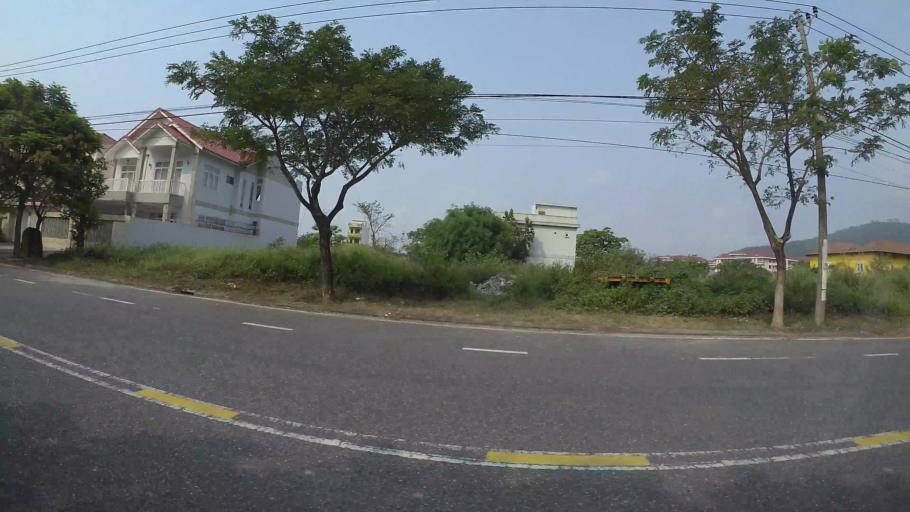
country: VN
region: Da Nang
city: Son Tra
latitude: 16.1048
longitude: 108.2640
